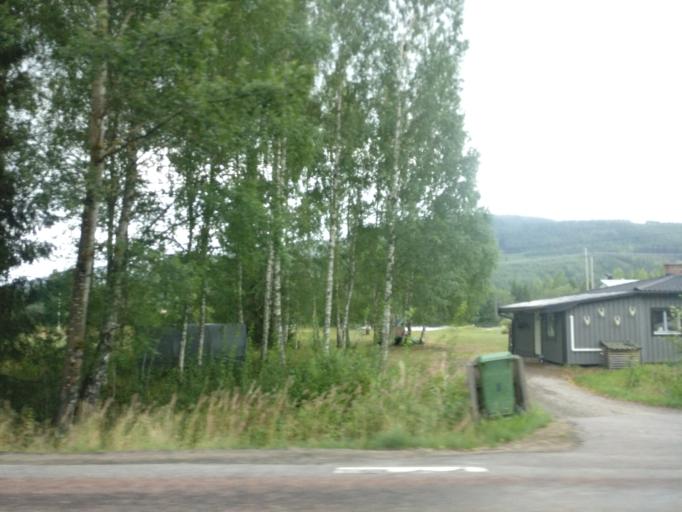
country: SE
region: Vaermland
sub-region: Torsby Kommun
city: Torsby
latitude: 60.7382
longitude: 12.8568
